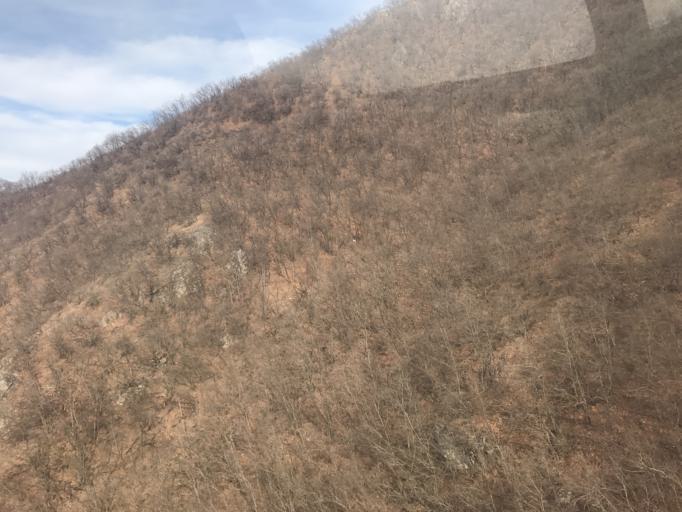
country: RU
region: Stavropol'skiy
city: Goryachevodskiy
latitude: 44.0467
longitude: 43.0850
